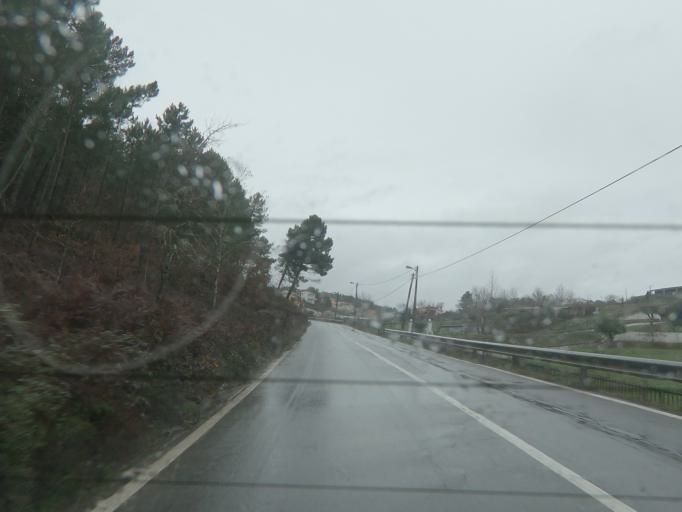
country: PT
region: Vila Real
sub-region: Vila Real
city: Vila Real
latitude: 41.2609
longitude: -7.6878
